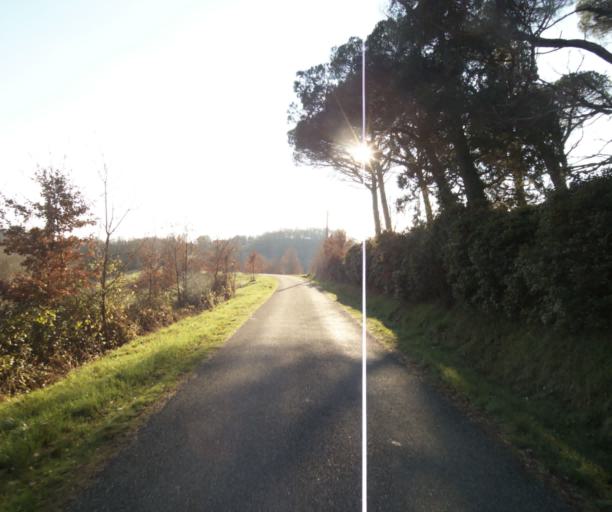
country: FR
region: Midi-Pyrenees
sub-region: Departement du Tarn-et-Garonne
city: Moissac
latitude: 44.1491
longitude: 1.1137
